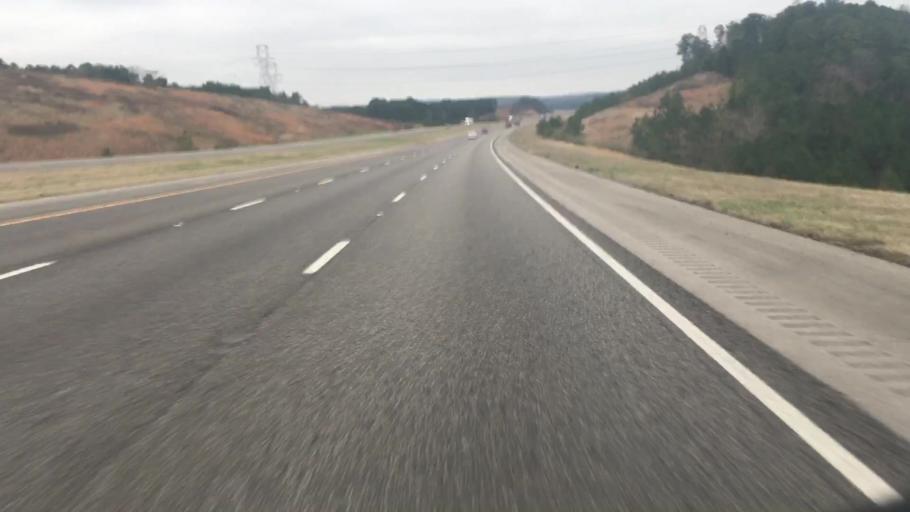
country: US
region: Alabama
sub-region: Jefferson County
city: Graysville
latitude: 33.6513
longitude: -87.0003
